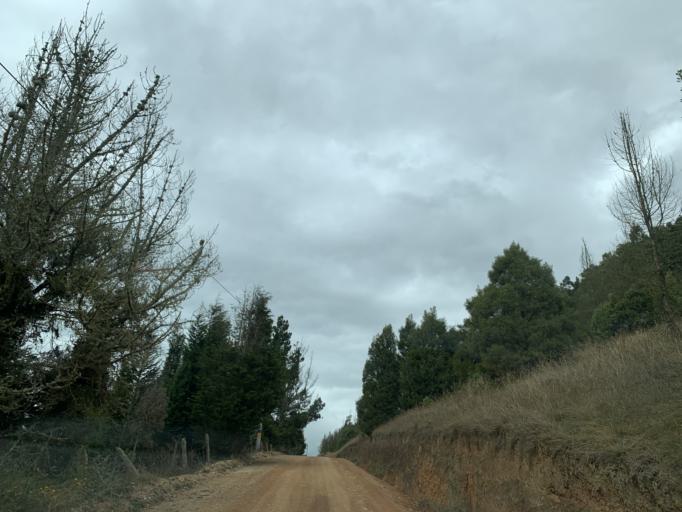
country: CO
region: Boyaca
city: Tunja
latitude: 5.5404
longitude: -73.3202
